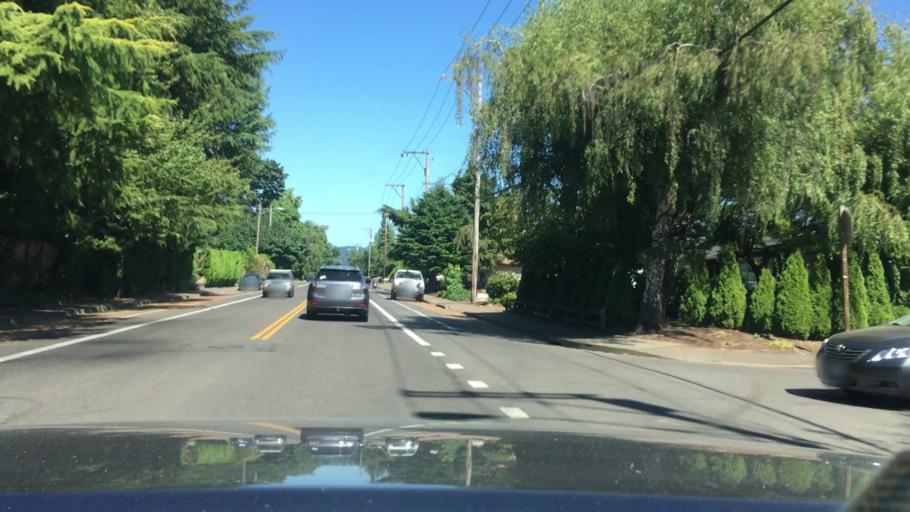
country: US
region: Oregon
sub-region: Lane County
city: Eugene
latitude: 44.0929
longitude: -123.0770
